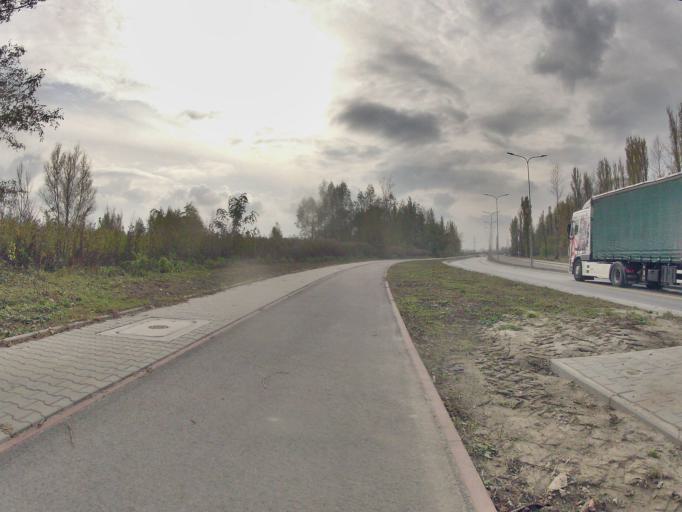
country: PL
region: Lesser Poland Voivodeship
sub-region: Powiat wielicki
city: Kokotow
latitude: 50.0670
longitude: 20.0903
